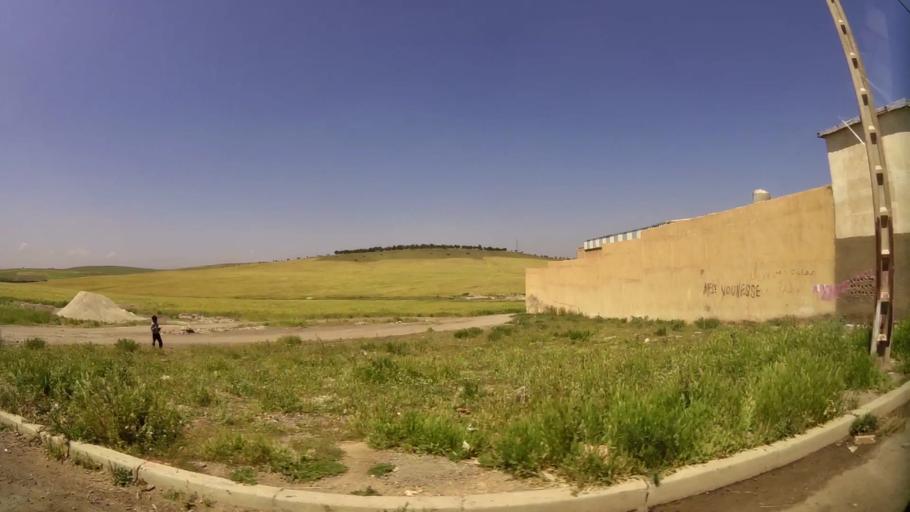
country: MA
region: Oriental
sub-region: Oujda-Angad
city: Oujda
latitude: 34.6823
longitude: -1.9606
